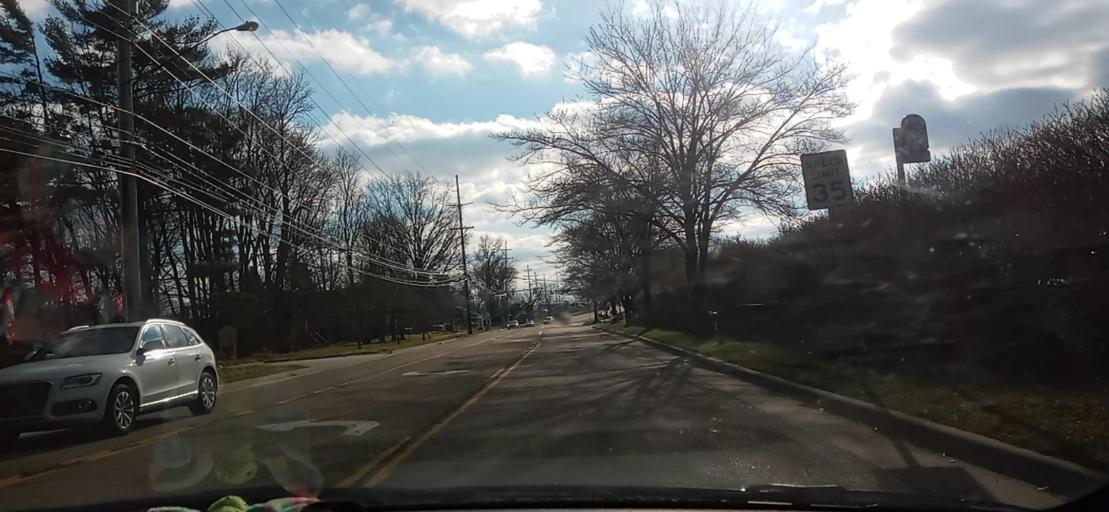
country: US
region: Ohio
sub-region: Summit County
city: Fairlawn
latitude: 41.1033
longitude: -81.5862
